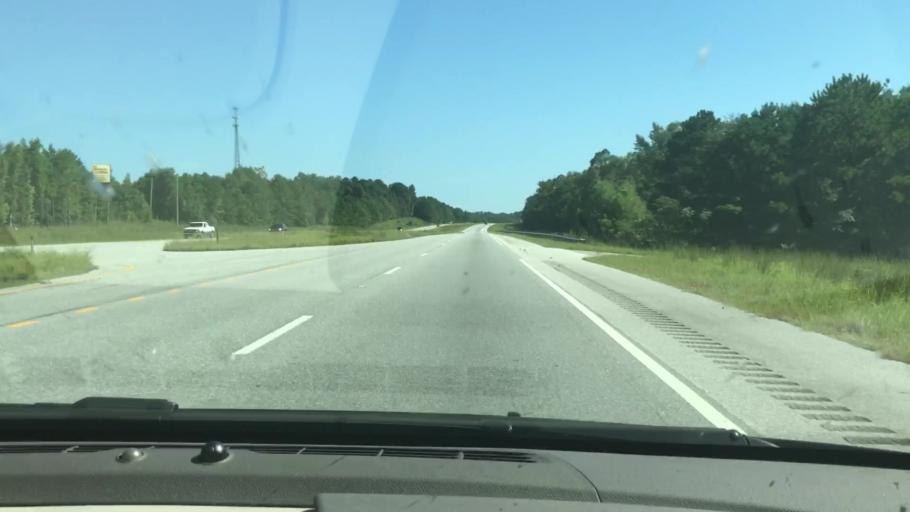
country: US
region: Alabama
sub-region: Russell County
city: Ladonia
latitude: 32.3848
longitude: -85.0804
